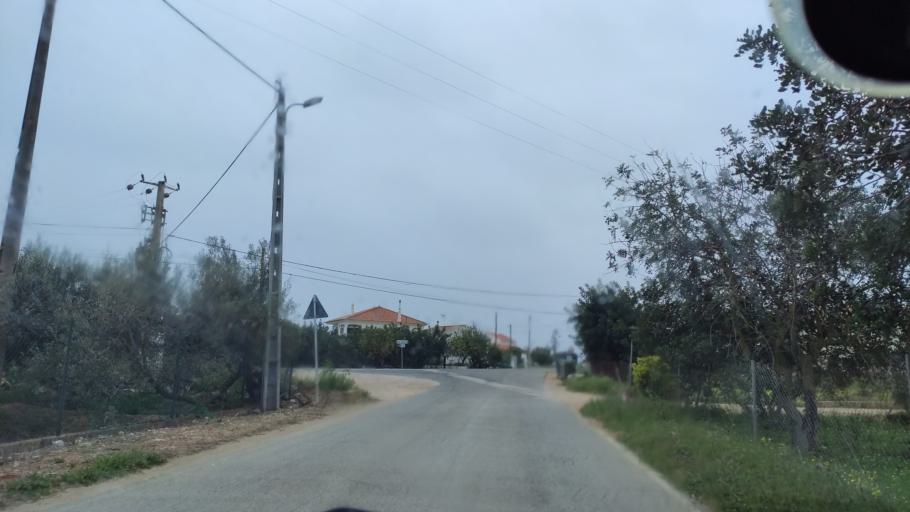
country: PT
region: Faro
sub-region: Faro
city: Santa Barbara de Nexe
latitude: 37.0778
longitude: -7.9305
